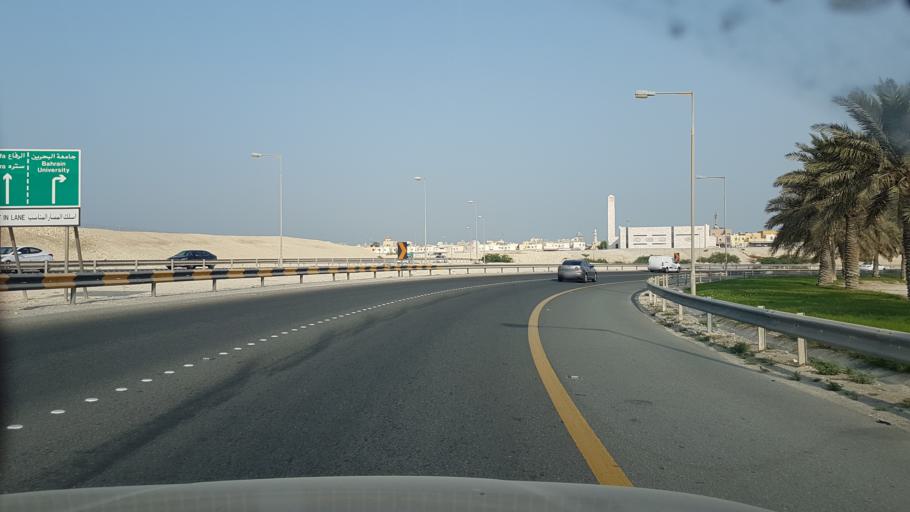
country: BH
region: Central Governorate
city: Dar Kulayb
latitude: 26.0565
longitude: 50.5167
